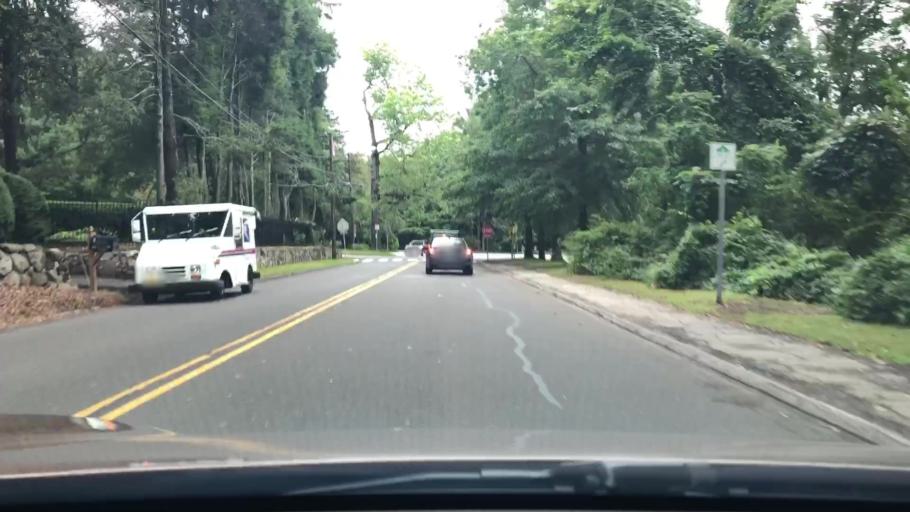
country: US
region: Connecticut
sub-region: Fairfield County
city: Darien
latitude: 41.1171
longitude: -73.4524
